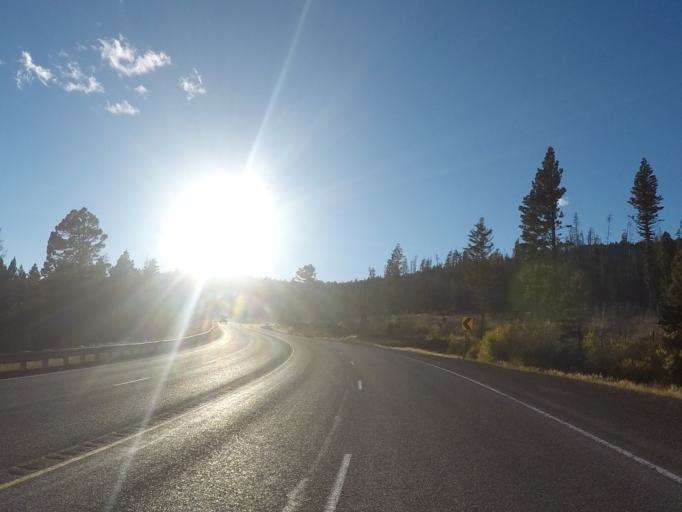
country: US
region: Montana
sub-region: Lewis and Clark County
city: Helena West Side
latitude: 46.5765
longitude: -112.2885
